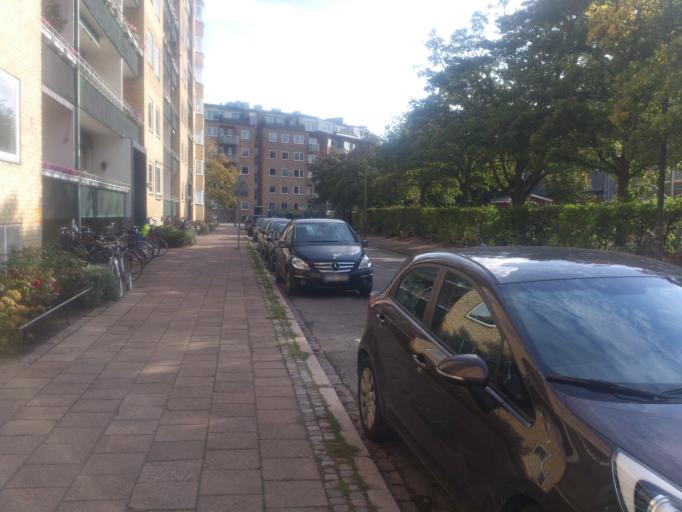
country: SE
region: Skane
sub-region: Malmo
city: Malmoe
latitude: 55.6001
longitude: 12.9717
